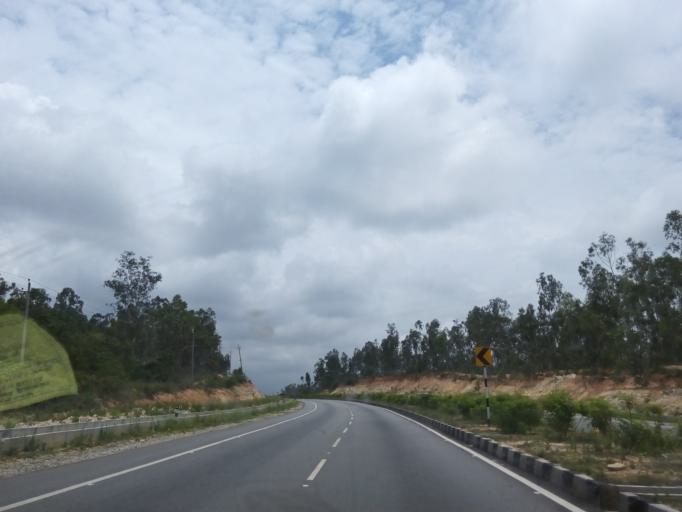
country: IN
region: Karnataka
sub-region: Hassan
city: Hassan
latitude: 12.9921
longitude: 76.1798
